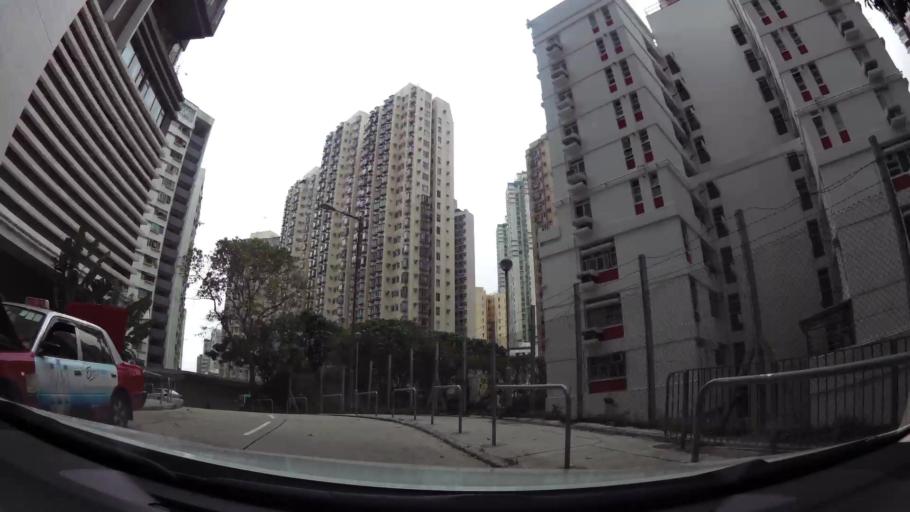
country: HK
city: Hong Kong
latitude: 22.2793
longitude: 114.1287
